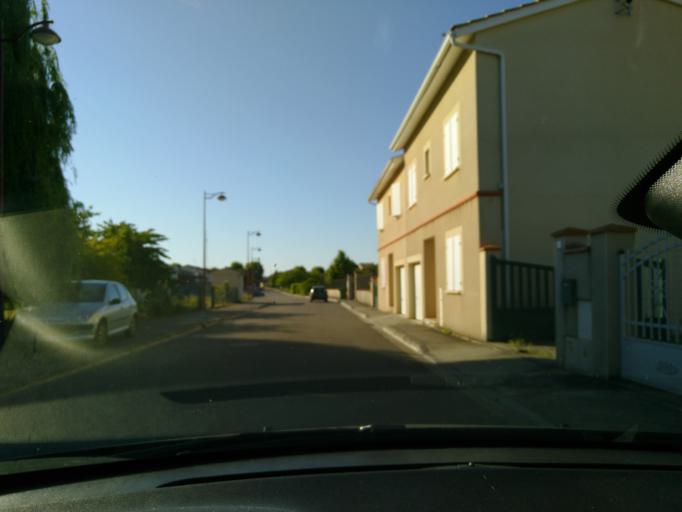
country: FR
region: Midi-Pyrenees
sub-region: Departement de la Haute-Garonne
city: Grenade
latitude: 43.7674
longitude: 1.2940
